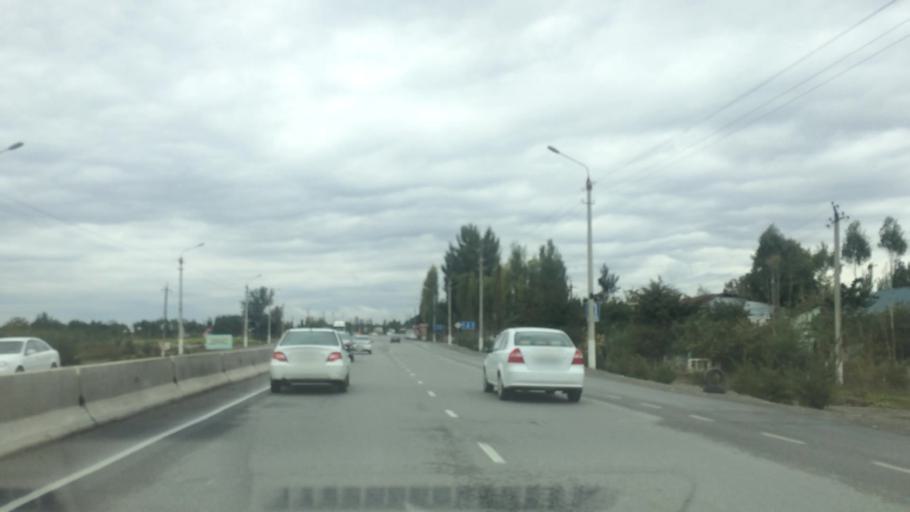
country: UZ
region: Jizzax
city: Jizzax
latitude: 39.9817
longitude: 67.5705
